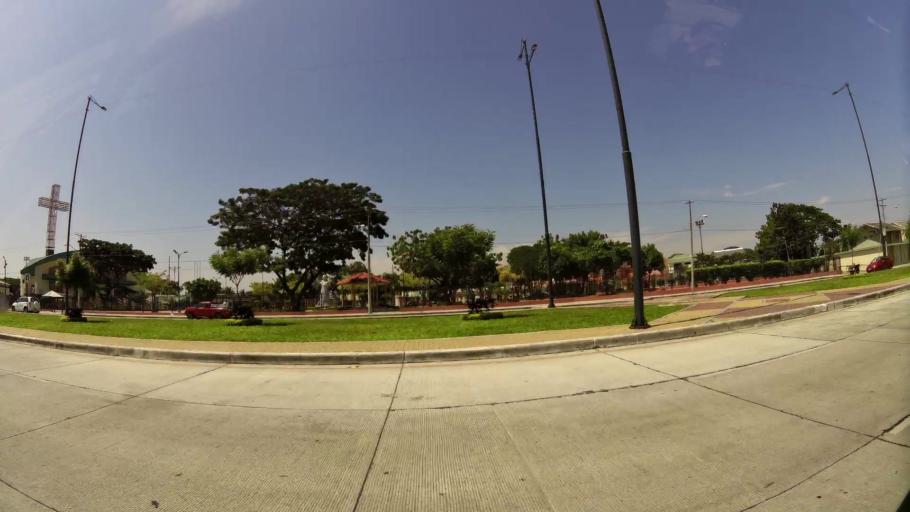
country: EC
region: Guayas
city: Eloy Alfaro
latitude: -2.1096
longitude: -79.8989
